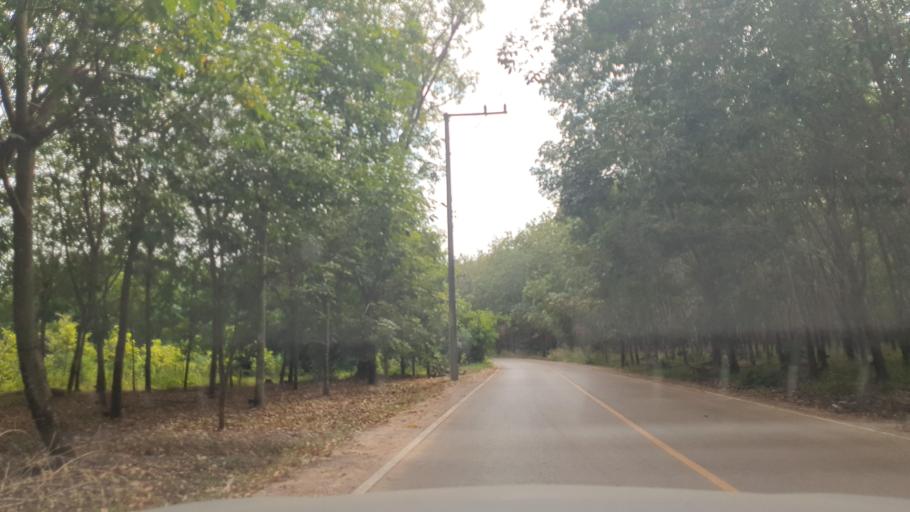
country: TH
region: Changwat Bueng Kan
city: Si Wilai
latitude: 18.2801
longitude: 103.7932
